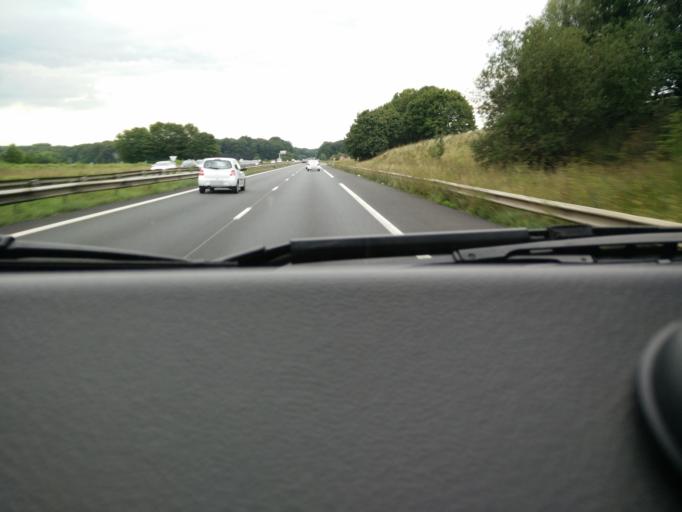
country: FR
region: Nord-Pas-de-Calais
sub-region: Departement du Nord
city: Aubry-du-Hainaut
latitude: 50.3781
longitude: 3.4704
